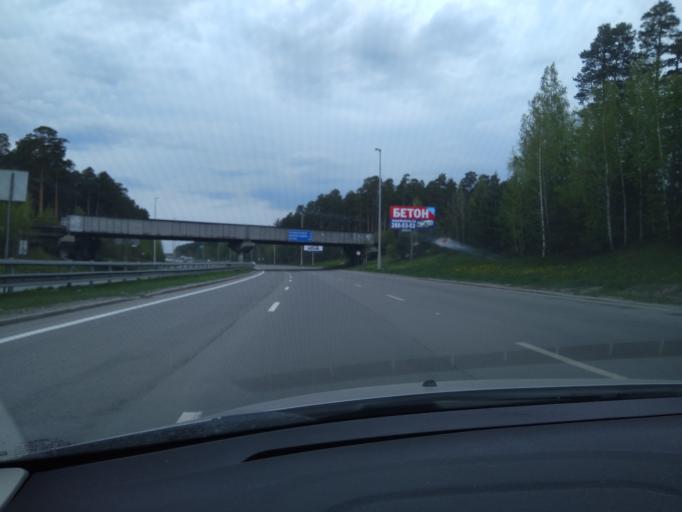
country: RU
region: Sverdlovsk
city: Yekaterinburg
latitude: 56.8862
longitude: 60.5522
